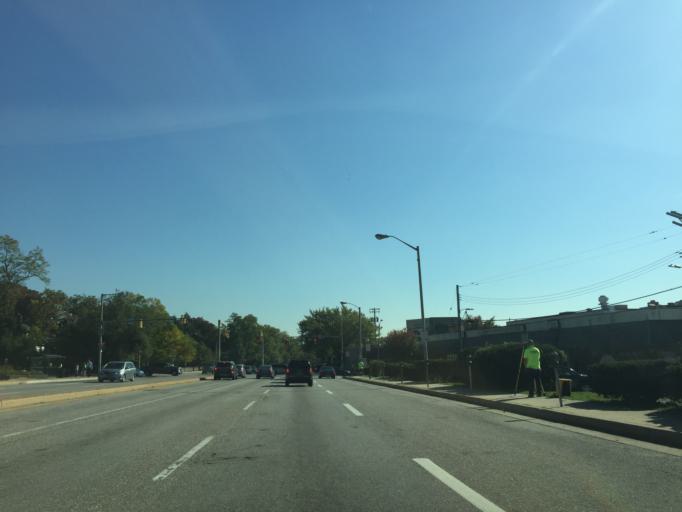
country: US
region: Maryland
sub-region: Baltimore County
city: Towson
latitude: 39.3650
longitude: -76.6110
